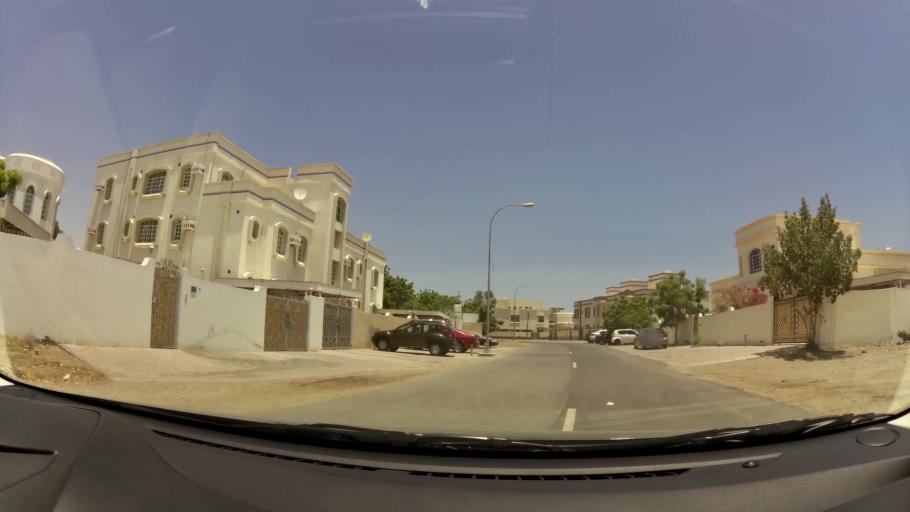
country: OM
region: Muhafazat Masqat
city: As Sib al Jadidah
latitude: 23.6271
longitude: 58.2377
